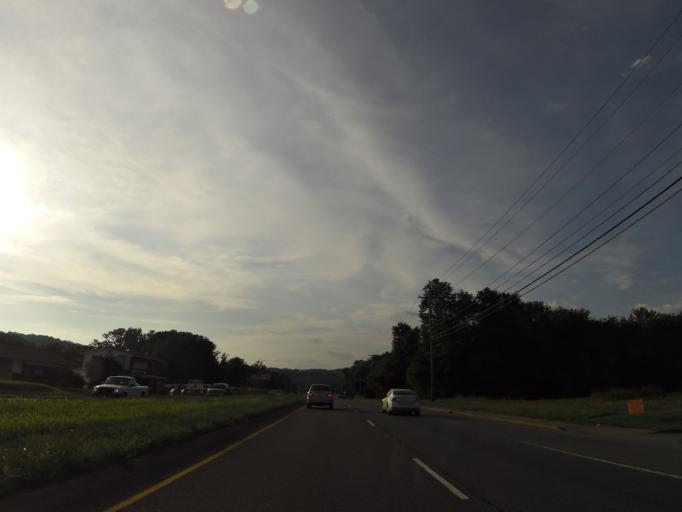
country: US
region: Tennessee
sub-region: Anderson County
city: Oak Ridge
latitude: 35.9840
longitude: -84.1848
